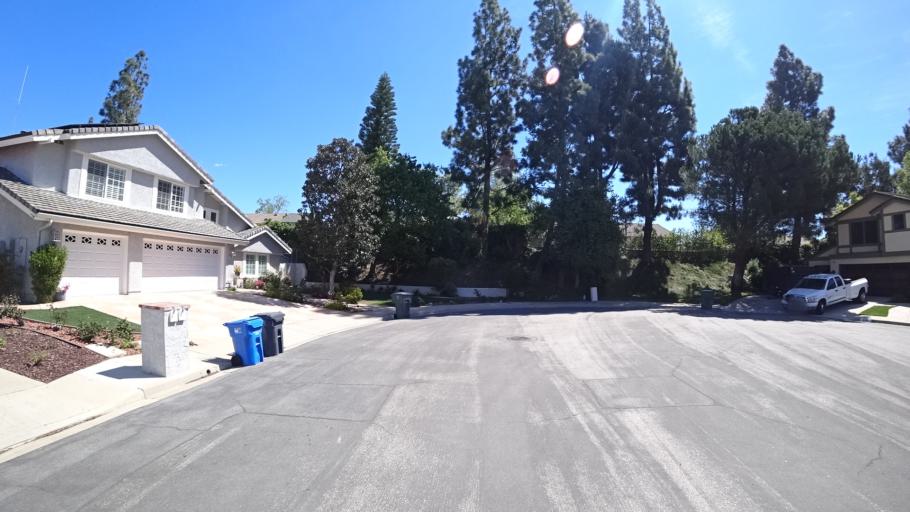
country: US
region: California
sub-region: Ventura County
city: Thousand Oaks
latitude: 34.2223
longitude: -118.8729
